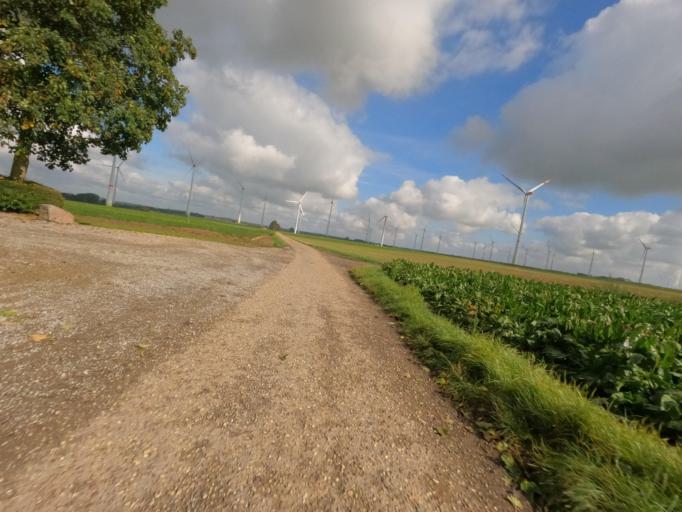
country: DE
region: North Rhine-Westphalia
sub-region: Regierungsbezirk Koln
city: Linnich
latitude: 51.0082
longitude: 6.2898
